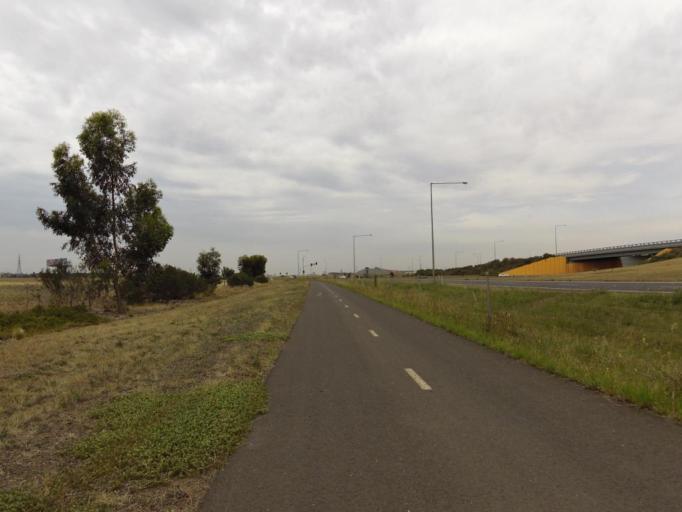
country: AU
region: Victoria
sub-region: Melton
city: Caroline Springs
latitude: -37.7603
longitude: 144.7408
